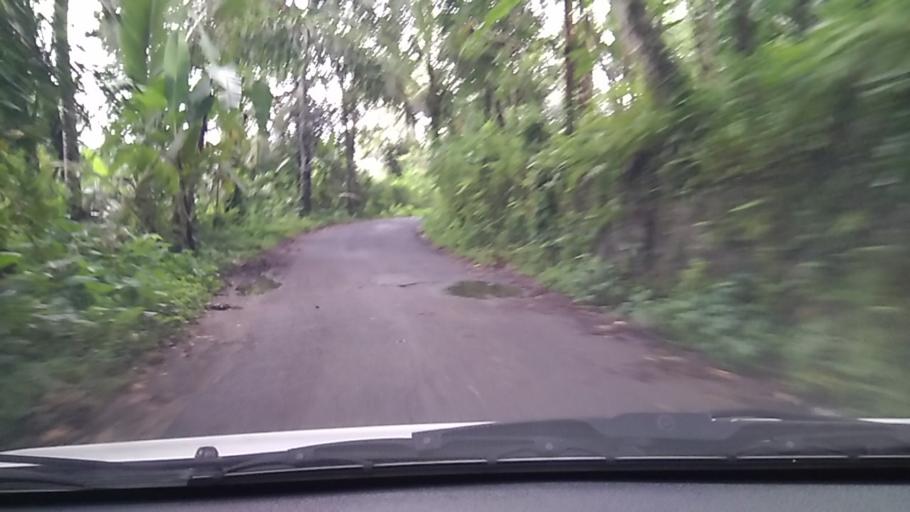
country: ID
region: Bali
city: Banjar Dujung Kaja
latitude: -8.4089
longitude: 115.2884
